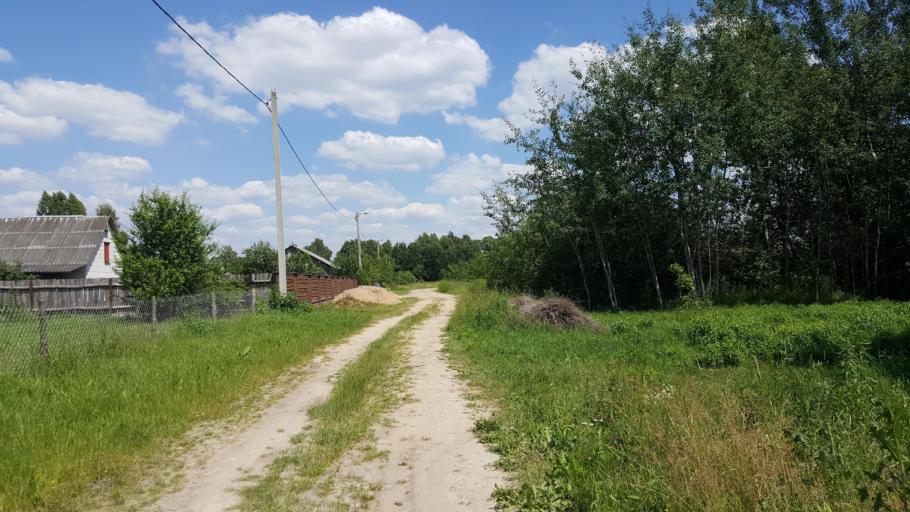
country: BY
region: Brest
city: Kamyanyets
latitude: 52.4133
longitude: 23.8323
